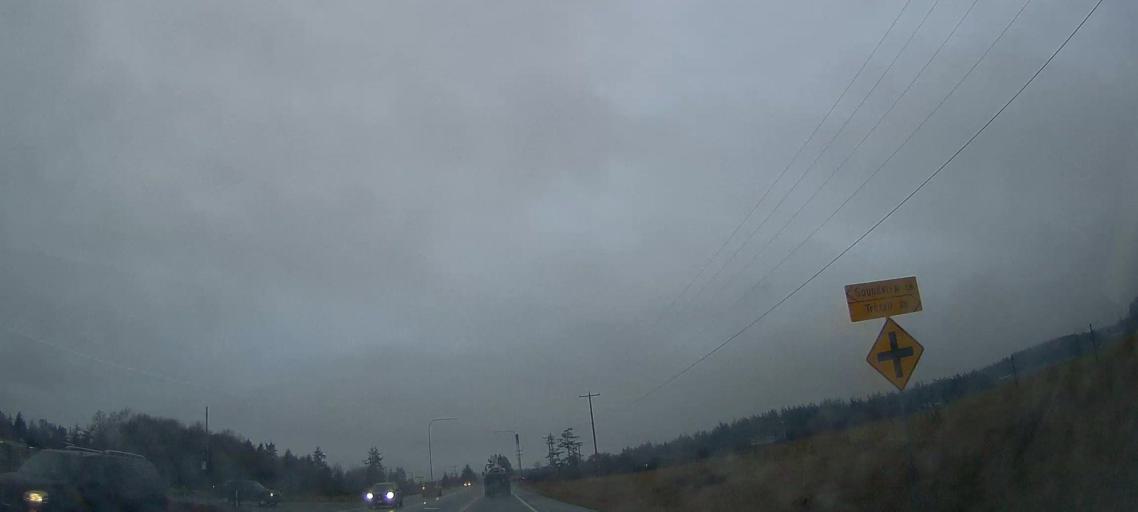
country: US
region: Washington
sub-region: Island County
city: Ault Field
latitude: 48.3752
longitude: -122.6520
